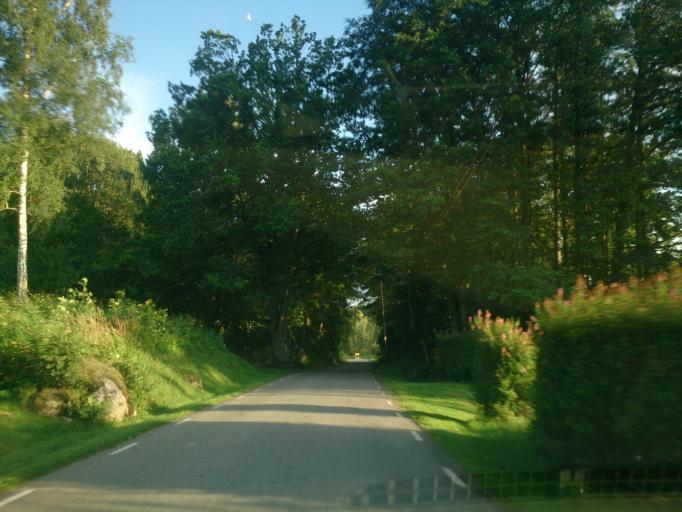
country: SE
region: OEstergoetland
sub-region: Atvidabergs Kommun
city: Atvidaberg
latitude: 58.3089
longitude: 16.0770
